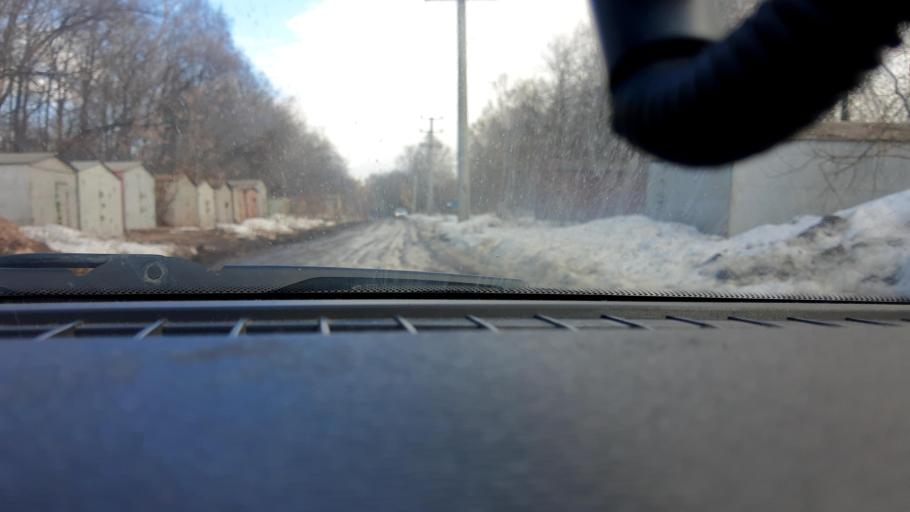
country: RU
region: Bashkortostan
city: Iglino
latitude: 54.7721
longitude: 56.2392
